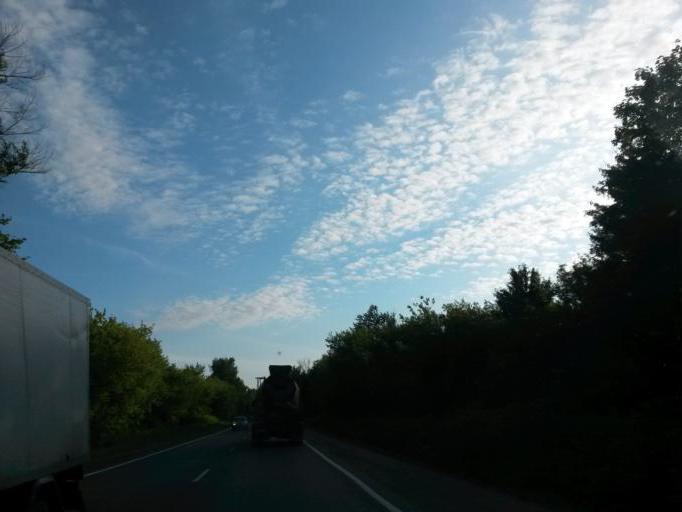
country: RU
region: Moskovskaya
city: Yam
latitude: 55.4588
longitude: 37.6879
